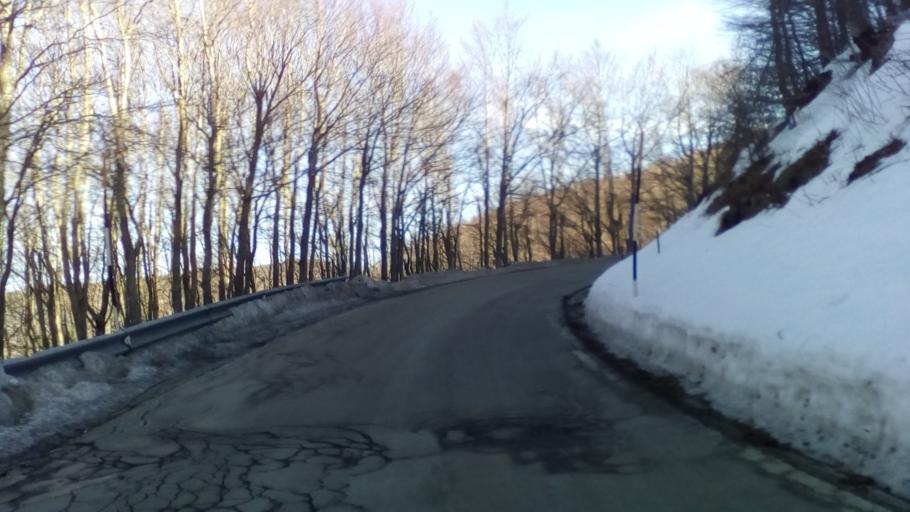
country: IT
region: Tuscany
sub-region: Provincia di Lucca
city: Castiglione di Garfagnana
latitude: 44.1942
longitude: 10.4830
